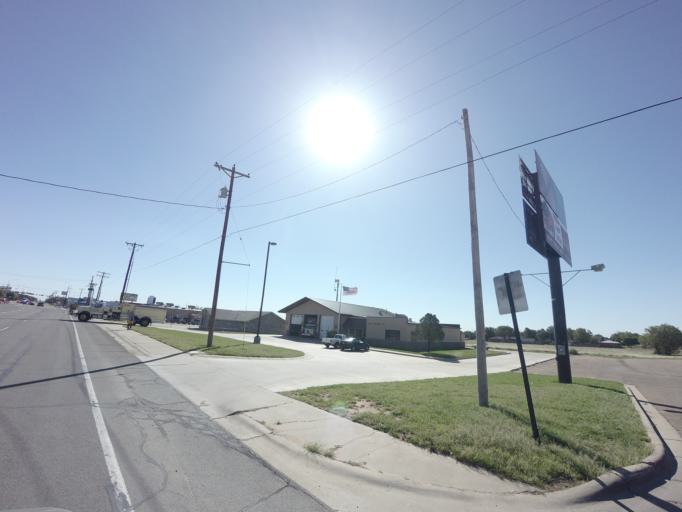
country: US
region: New Mexico
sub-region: Curry County
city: Clovis
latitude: 34.4338
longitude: -103.1987
